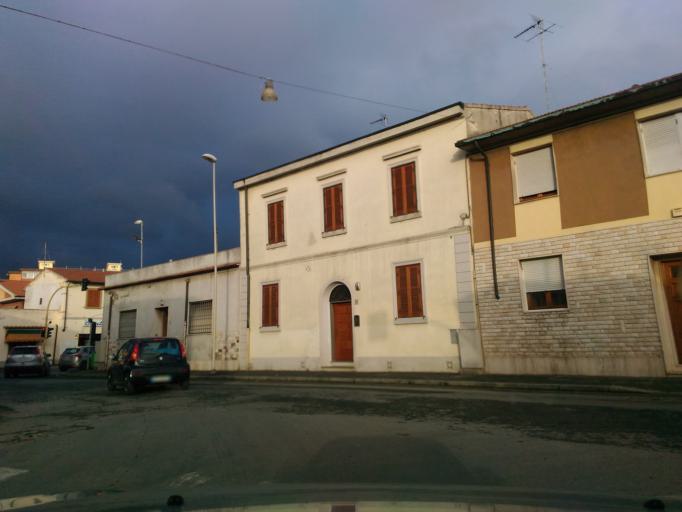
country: IT
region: Tuscany
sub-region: Provincia di Livorno
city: Livorno
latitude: 43.5631
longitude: 10.3301
